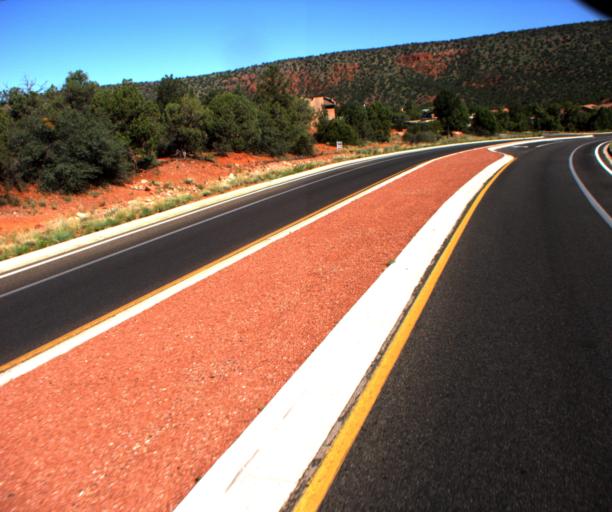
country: US
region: Arizona
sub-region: Coconino County
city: Sedona
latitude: 34.8355
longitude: -111.7769
